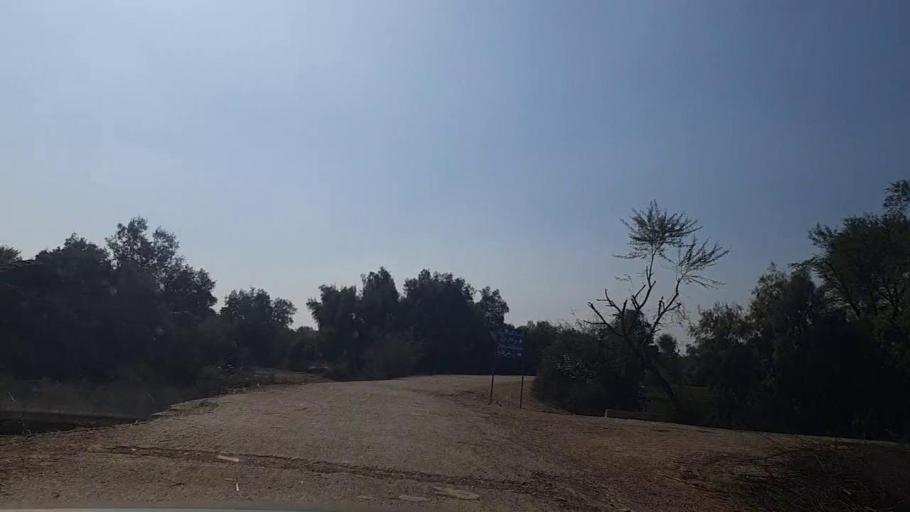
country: PK
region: Sindh
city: Sehwan
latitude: 26.2793
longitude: 68.0391
